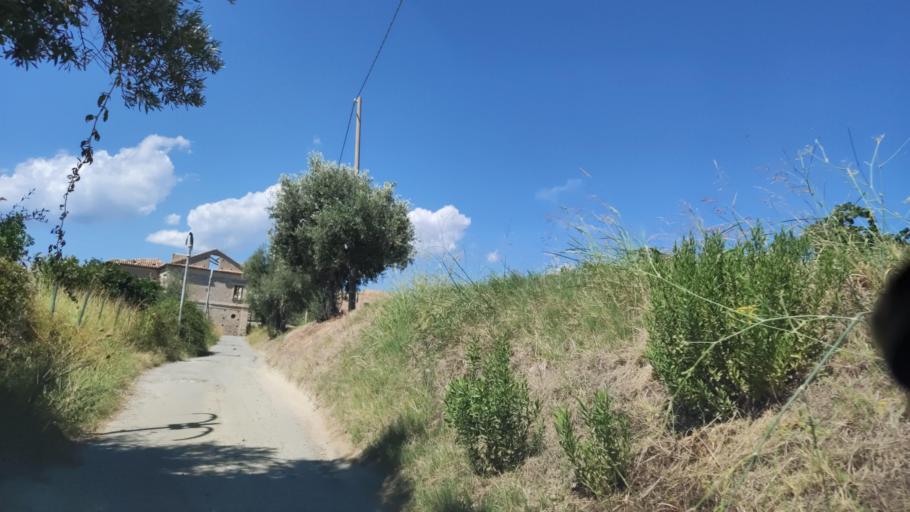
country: IT
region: Calabria
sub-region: Provincia di Reggio Calabria
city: Monasterace
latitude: 38.4401
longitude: 16.5543
